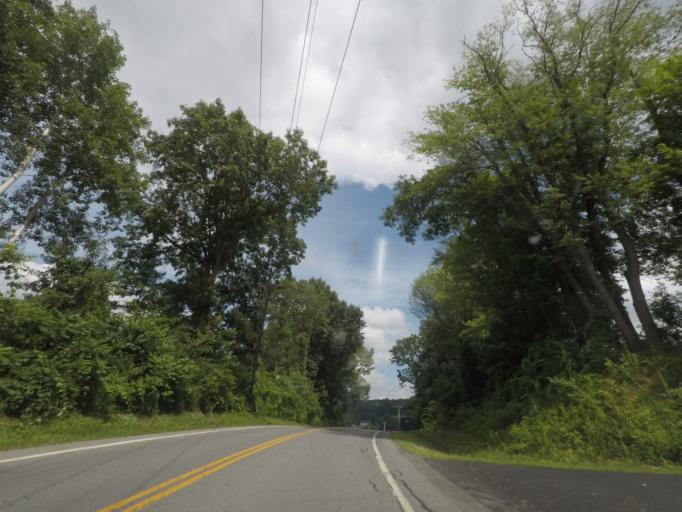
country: US
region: New York
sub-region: Saratoga County
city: Stillwater
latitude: 43.0238
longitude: -73.6981
